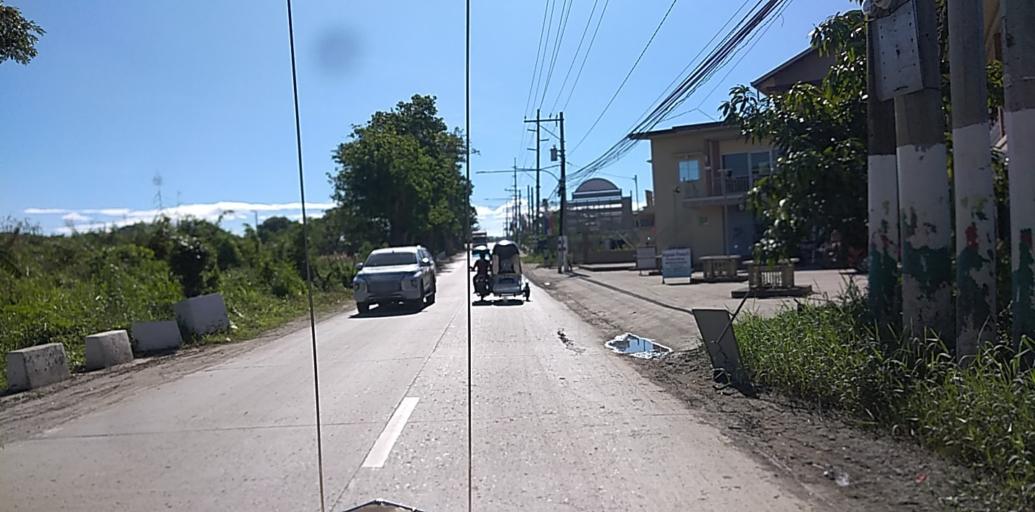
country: PH
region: Central Luzon
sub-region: Province of Pampanga
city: San Luis
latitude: 15.0461
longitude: 120.7866
